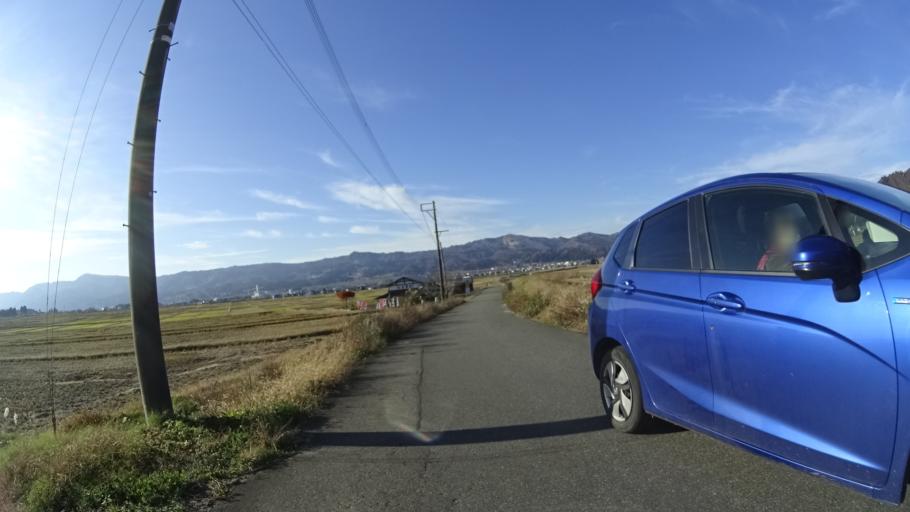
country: JP
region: Niigata
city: Muikamachi
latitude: 37.0356
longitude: 138.8879
